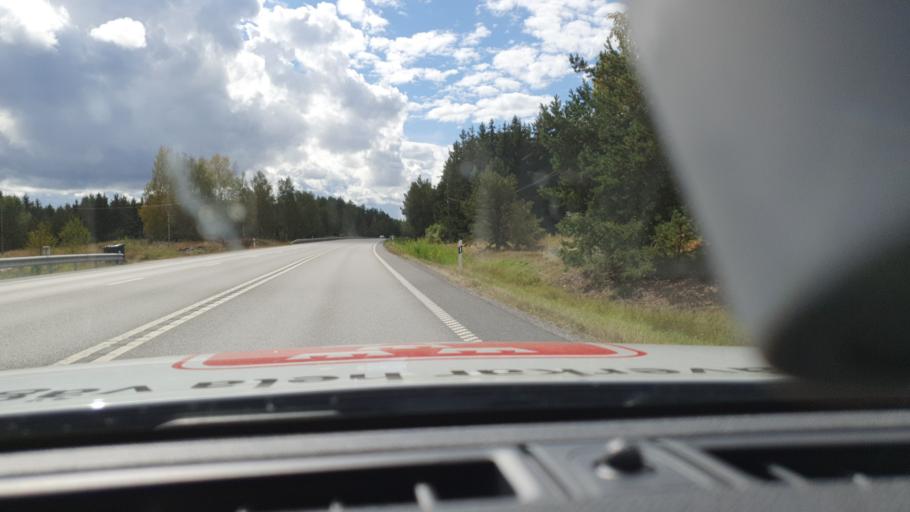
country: SE
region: Stockholm
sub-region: Osterakers Kommun
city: Akersberga
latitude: 59.4430
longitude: 18.2224
